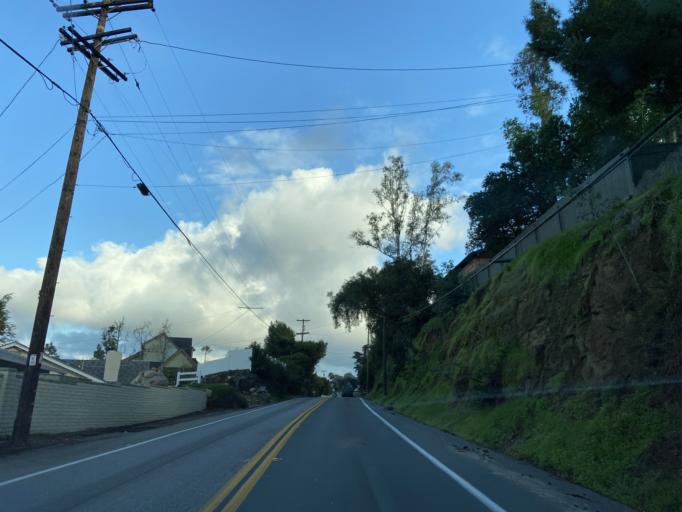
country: US
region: California
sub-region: San Diego County
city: La Mesa
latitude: 32.7777
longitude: -116.9952
